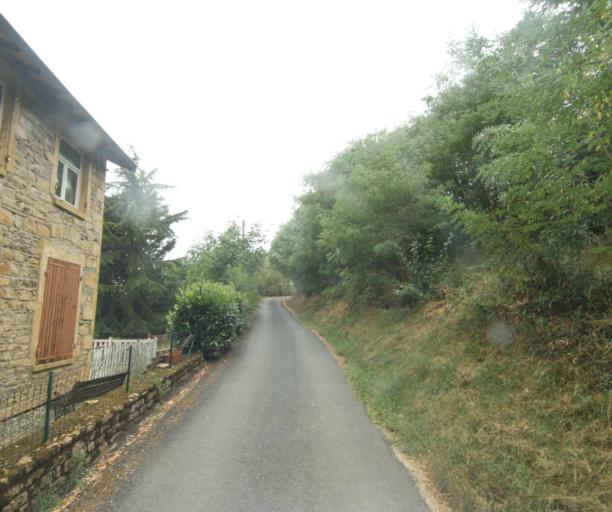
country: FR
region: Rhone-Alpes
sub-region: Departement du Rhone
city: Chatillon
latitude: 45.8798
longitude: 4.5959
